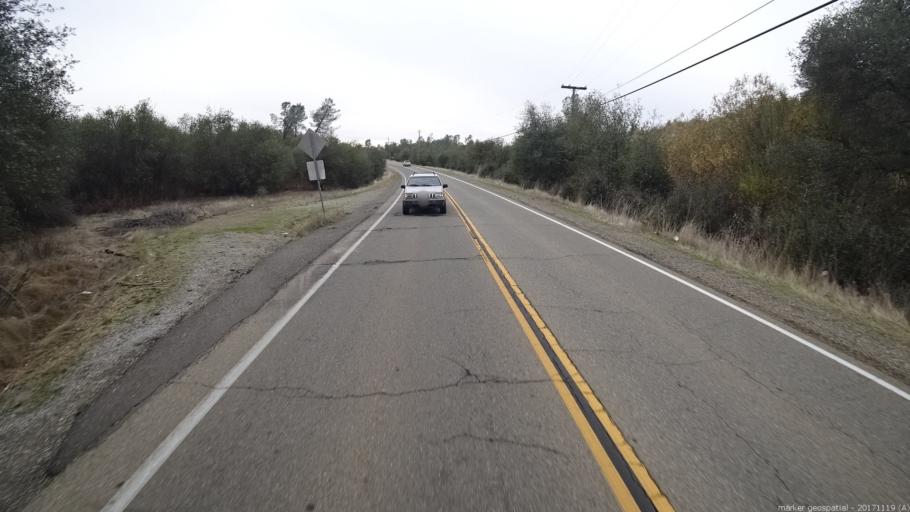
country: US
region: California
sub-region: Shasta County
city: Redding
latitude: 40.4851
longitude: -122.3956
